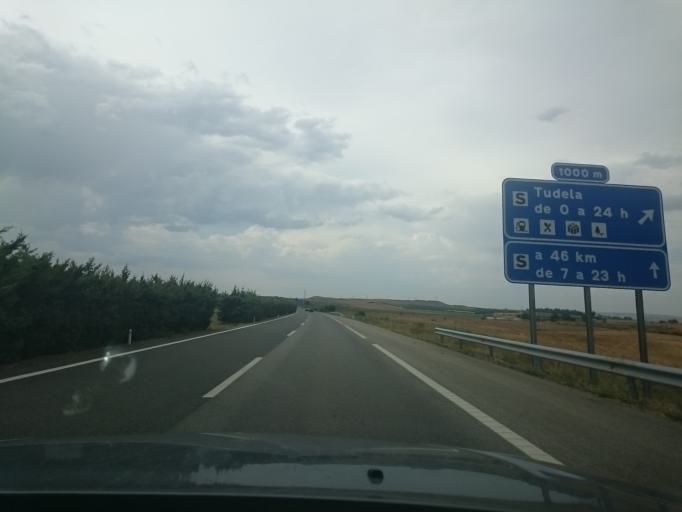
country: ES
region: Navarre
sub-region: Provincia de Navarra
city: Fontellas
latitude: 42.0031
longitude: -1.5850
